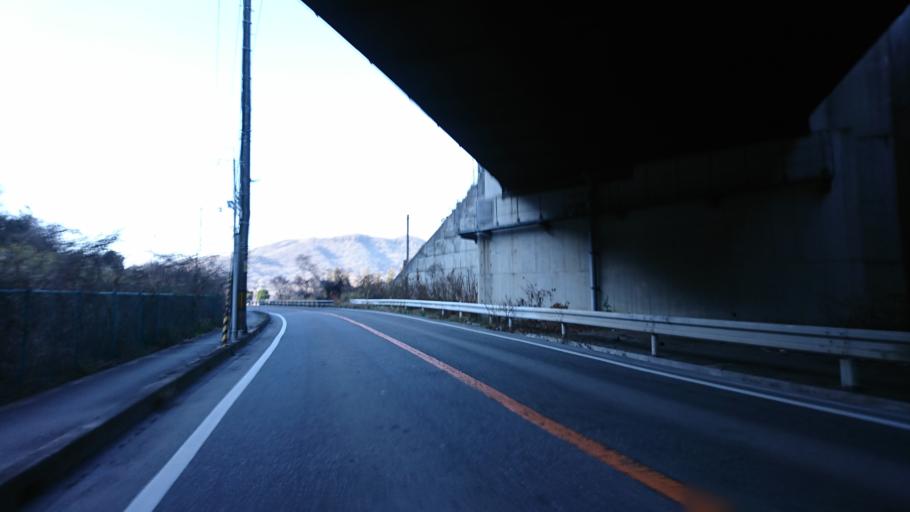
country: JP
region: Hyogo
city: Kakogawacho-honmachi
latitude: 34.8512
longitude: 134.8394
